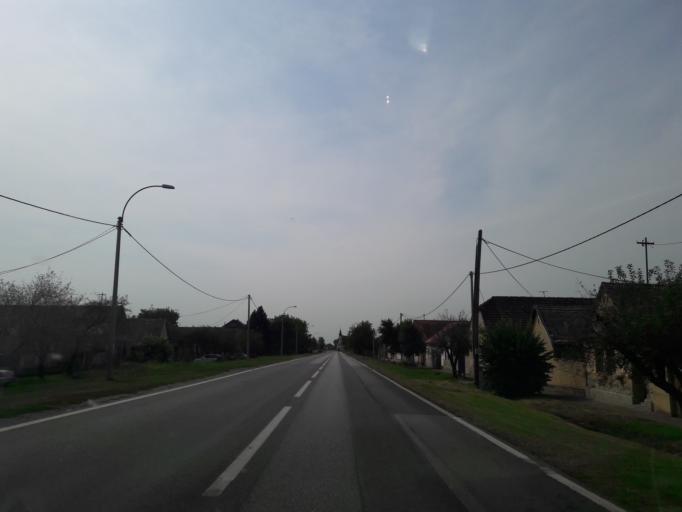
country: HR
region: Vukovarsko-Srijemska
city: Brsadin
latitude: 45.3618
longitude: 18.9129
